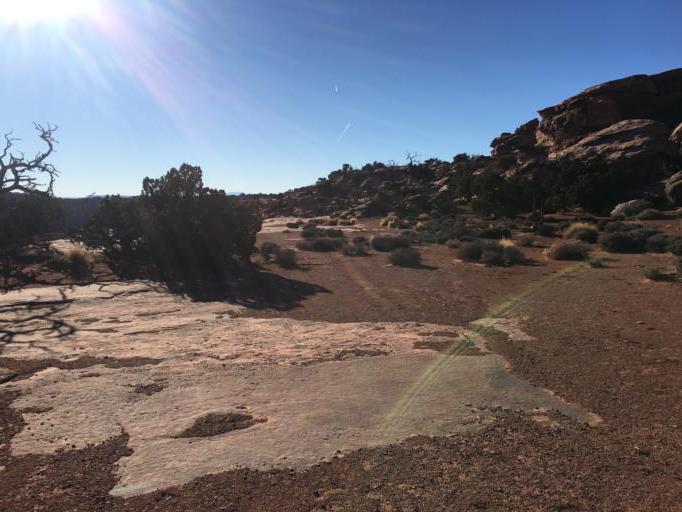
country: US
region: Utah
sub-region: Grand County
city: Moab
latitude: 38.3100
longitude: -109.8576
